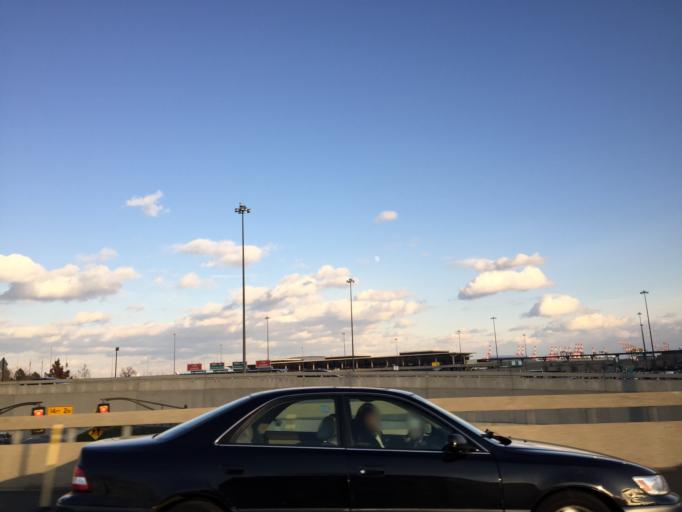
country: US
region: New Jersey
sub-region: Union County
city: Elizabeth
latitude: 40.6899
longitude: -74.1844
